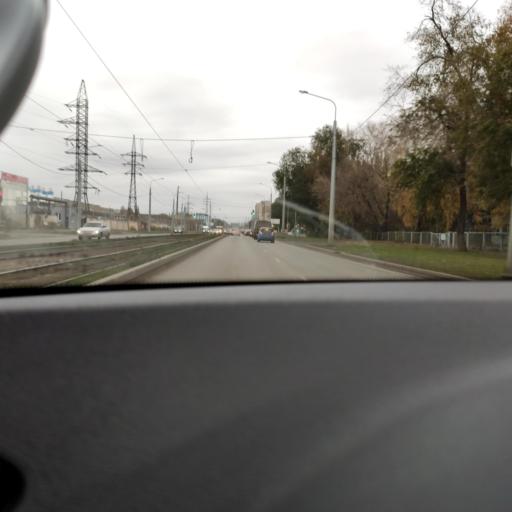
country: RU
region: Samara
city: Samara
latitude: 53.2016
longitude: 50.2622
